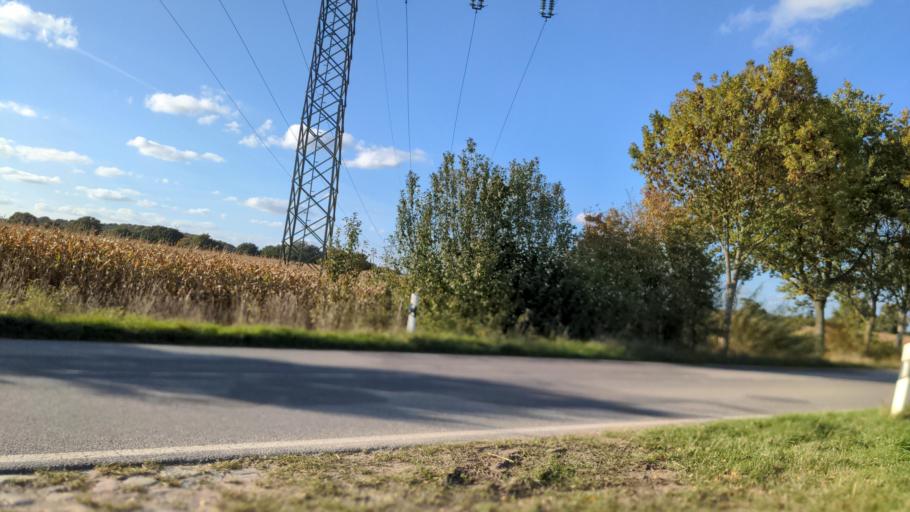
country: DE
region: Schleswig-Holstein
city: Heilshoop
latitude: 53.8992
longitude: 10.5246
